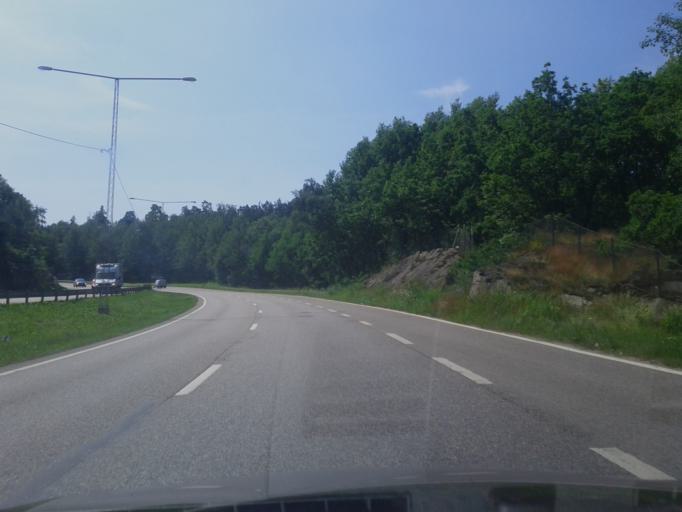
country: SE
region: Stockholm
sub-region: Huddinge Kommun
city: Huddinge
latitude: 59.2676
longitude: 18.0058
